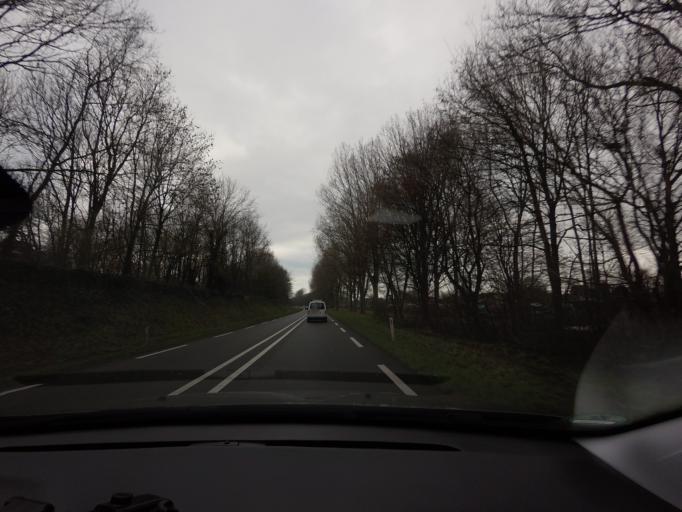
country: NL
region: South Holland
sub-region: Gemeente Alphen aan den Rijn
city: Alphen aan den Rijn
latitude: 52.1514
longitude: 4.6863
